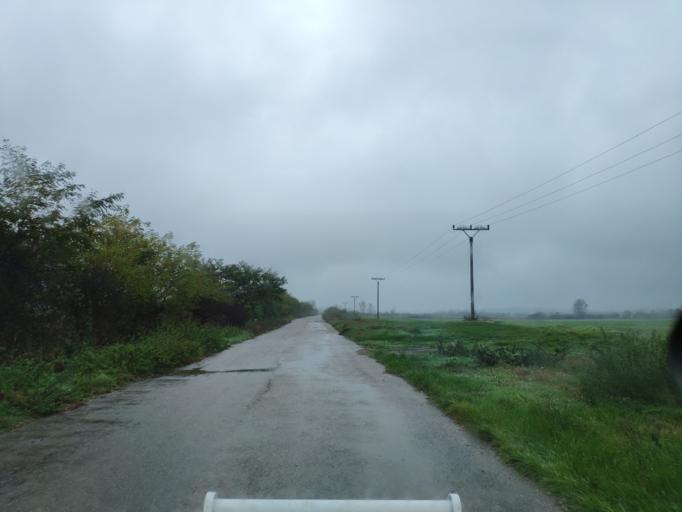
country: SK
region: Kosicky
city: Cierna nad Tisou
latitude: 48.4336
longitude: 22.0019
